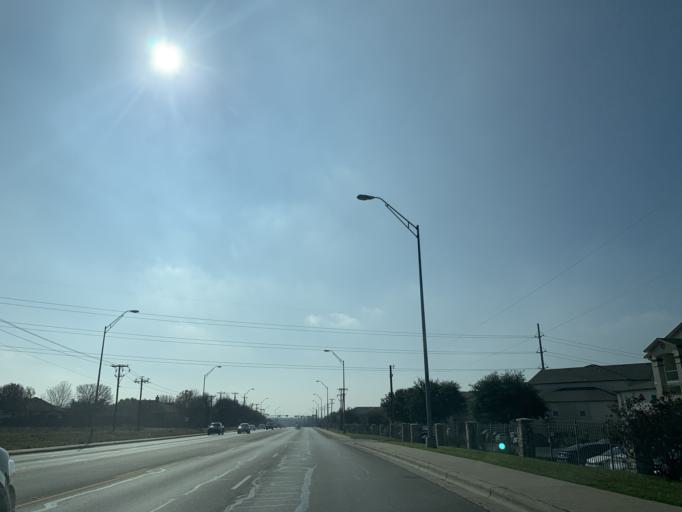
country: US
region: Texas
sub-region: Williamson County
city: Round Rock
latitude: 30.5423
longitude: -97.6506
